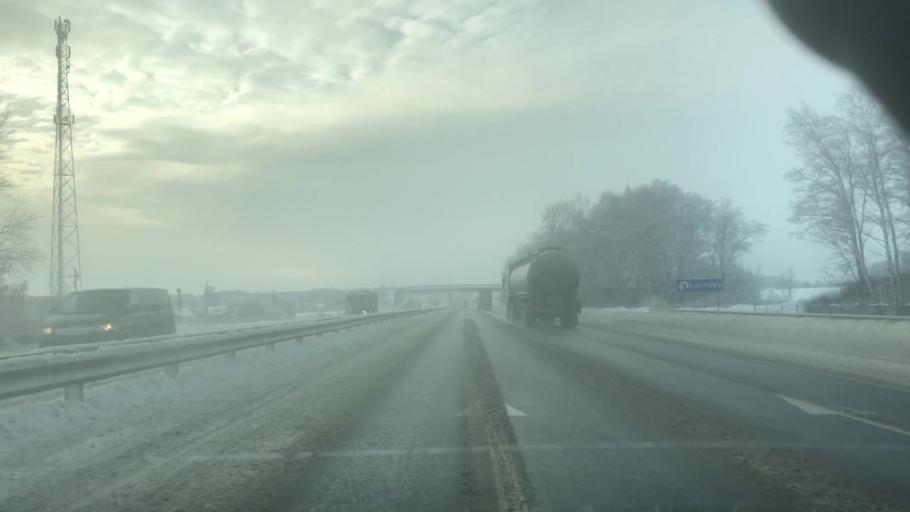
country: RU
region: Tula
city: Venev
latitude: 54.3972
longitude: 38.1597
